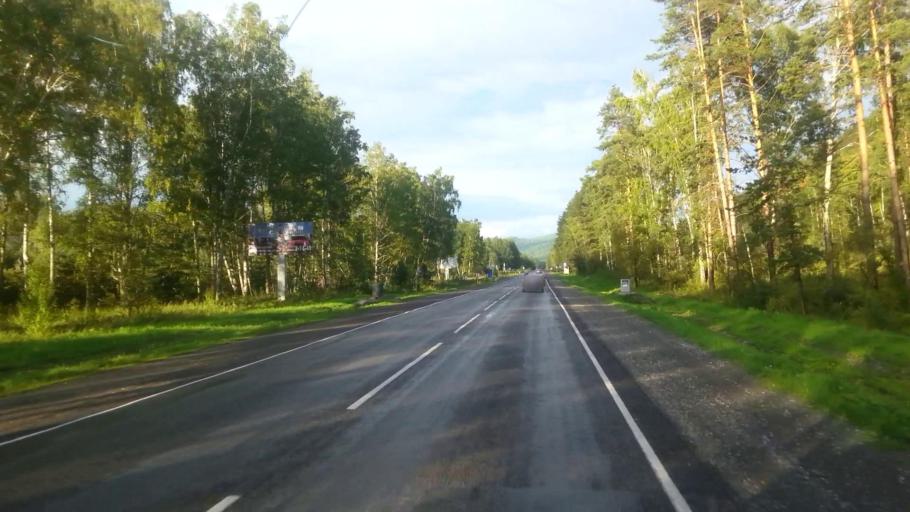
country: RU
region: Altay
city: Souzga
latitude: 51.8733
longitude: 85.7979
